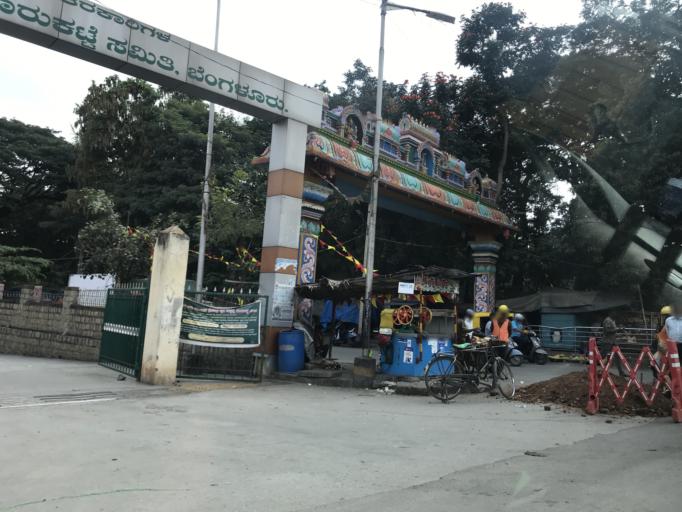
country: IN
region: Karnataka
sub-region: Bangalore Urban
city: Bangalore
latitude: 12.9649
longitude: 77.5621
